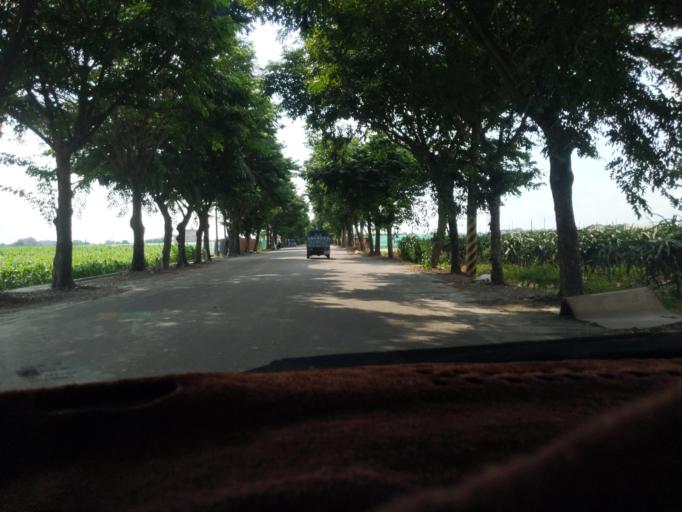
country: TW
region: Taiwan
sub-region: Yunlin
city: Douliu
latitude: 23.7870
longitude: 120.4088
